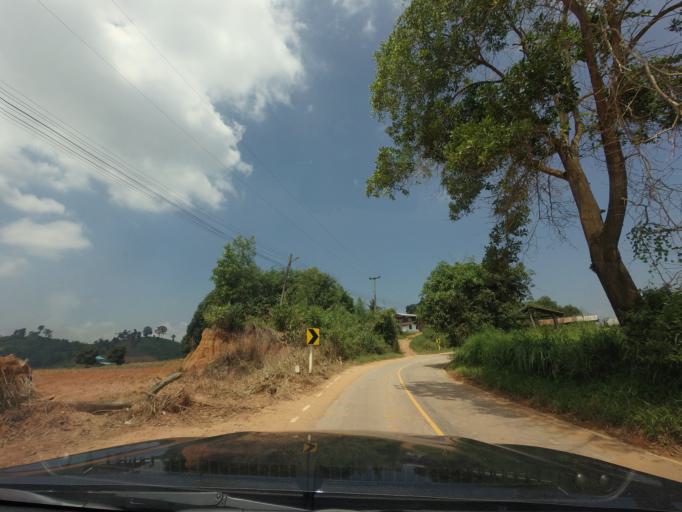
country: TH
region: Loei
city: Na Haeo
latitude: 17.5234
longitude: 100.8776
